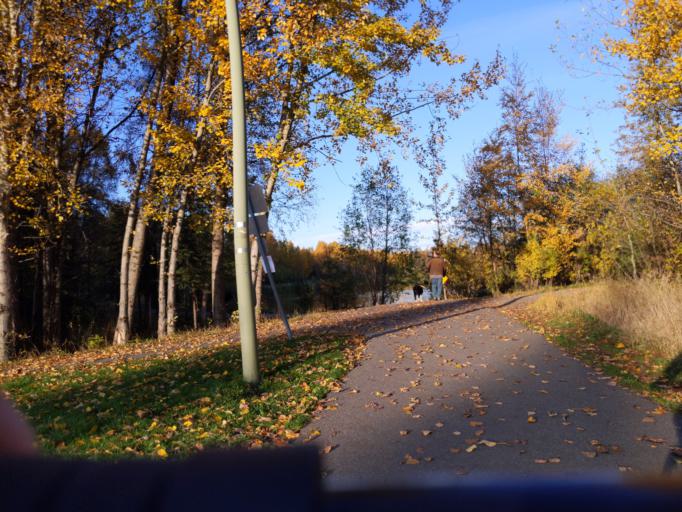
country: US
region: Alaska
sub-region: Anchorage Municipality
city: Anchorage
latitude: 61.1486
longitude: -149.8848
